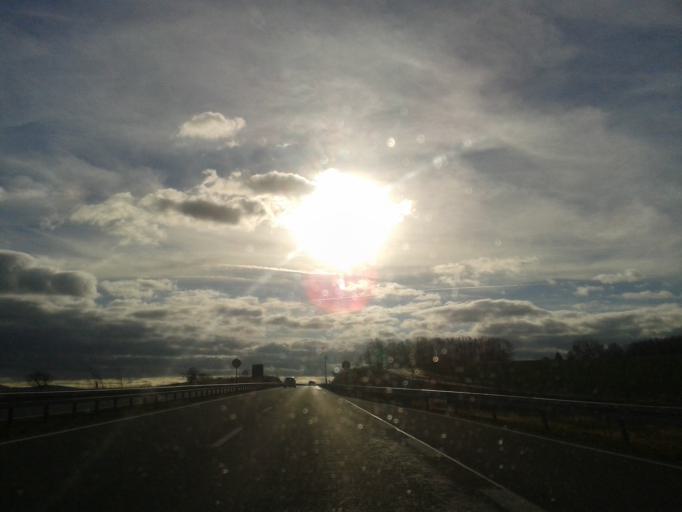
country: DE
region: Saxony
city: Weissenberg
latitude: 51.1488
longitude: 14.6542
